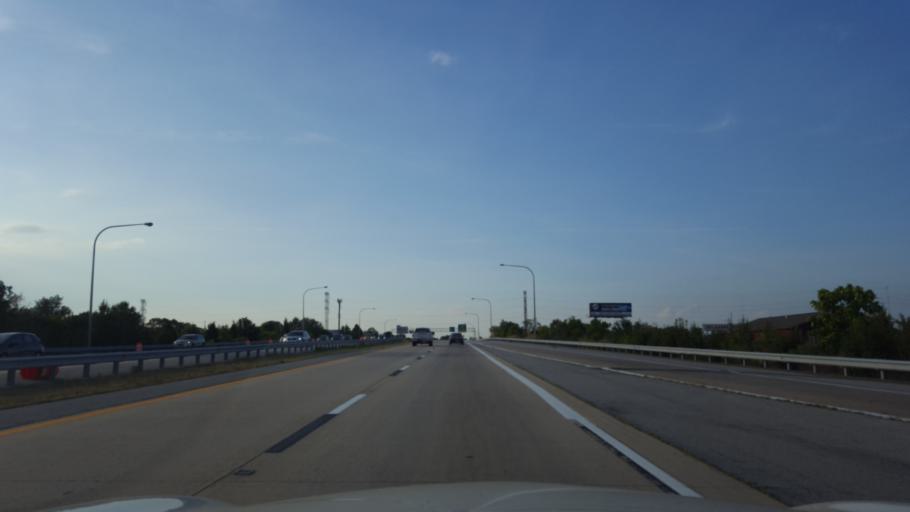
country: US
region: Delaware
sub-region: New Castle County
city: Newport
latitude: 39.7280
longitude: -75.6186
